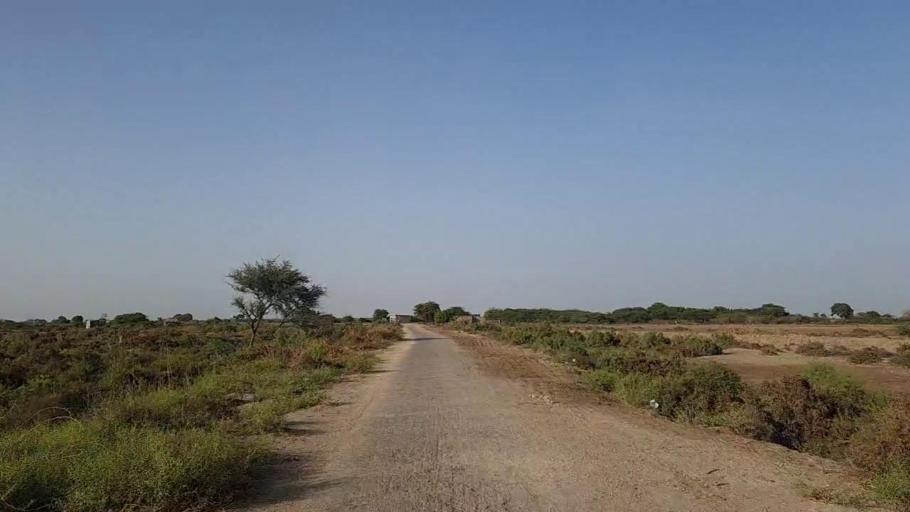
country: PK
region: Sindh
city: Jati
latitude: 24.3111
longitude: 68.1684
